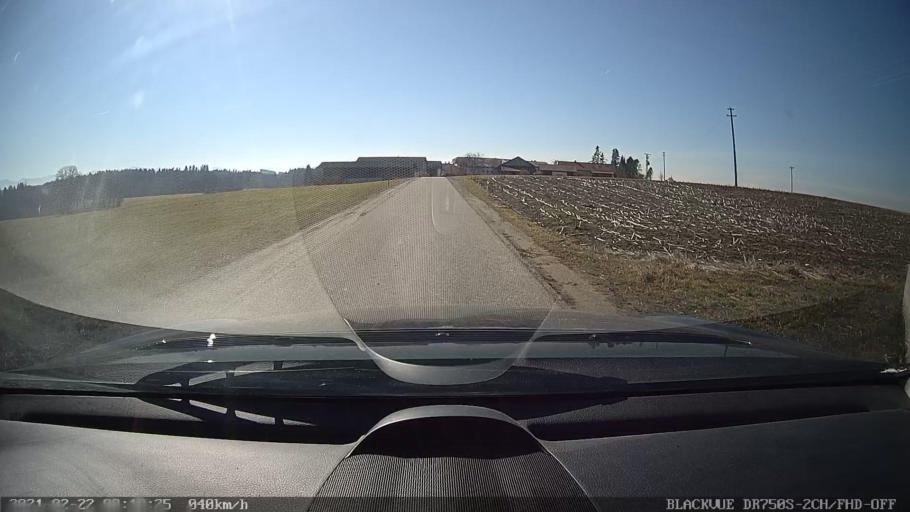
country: DE
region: Bavaria
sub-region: Upper Bavaria
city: Griesstatt
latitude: 47.9749
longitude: 12.1965
